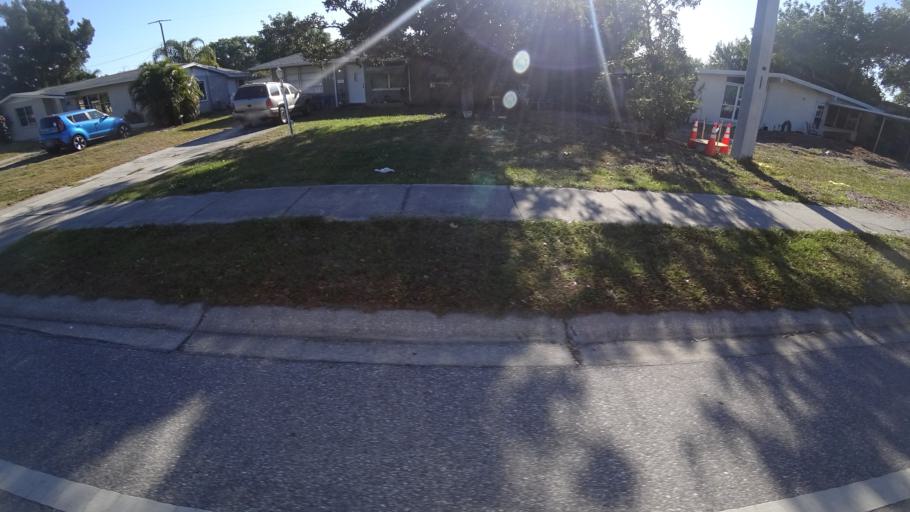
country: US
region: Florida
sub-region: Manatee County
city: Bayshore Gardens
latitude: 27.4239
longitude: -82.5878
